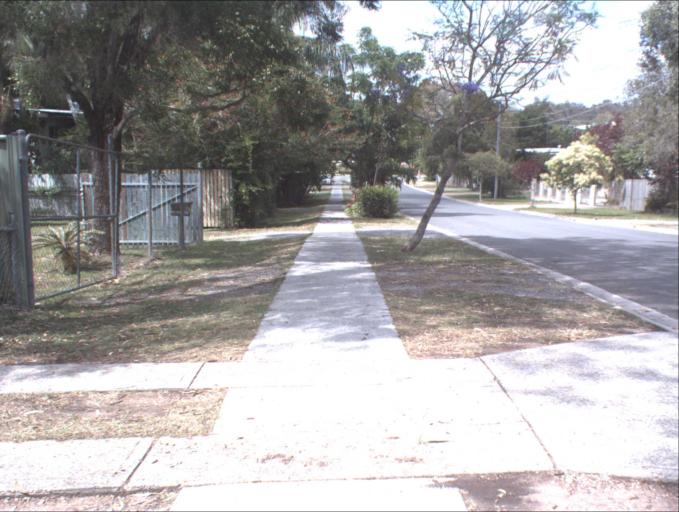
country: AU
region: Queensland
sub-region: Logan
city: Logan City
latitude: -27.6534
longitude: 153.1224
